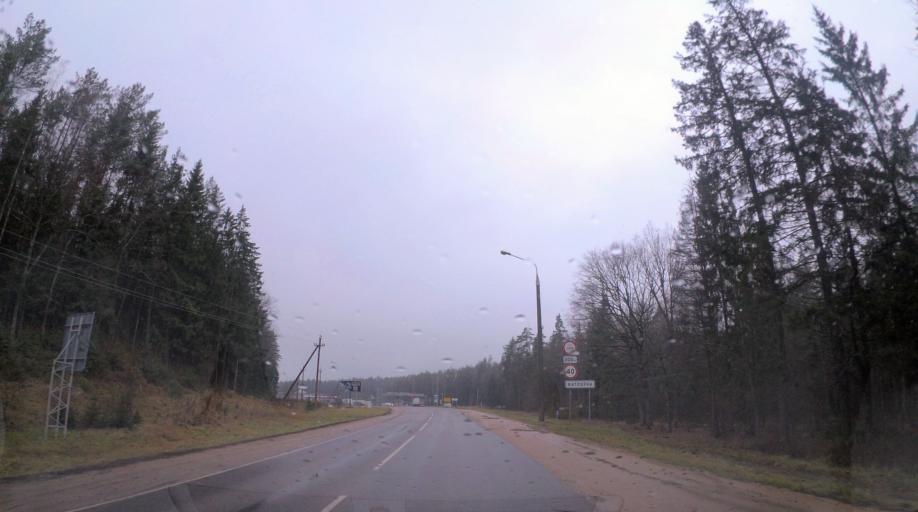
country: BY
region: Grodnenskaya
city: Astravyets
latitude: 54.7219
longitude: 25.7530
